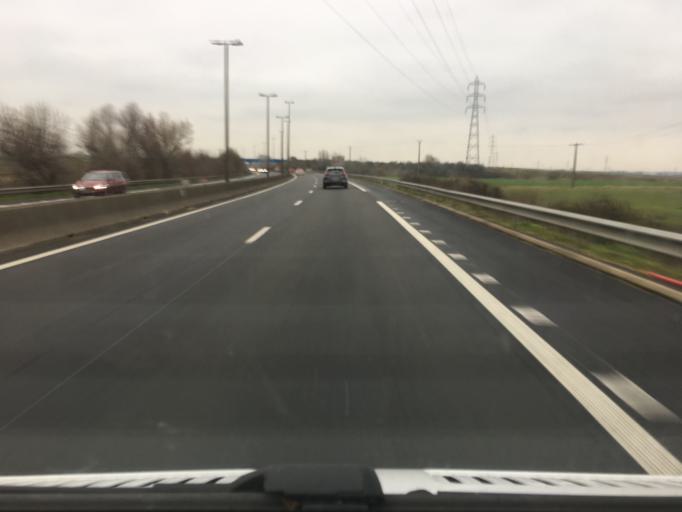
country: FR
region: Nord-Pas-de-Calais
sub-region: Departement du Nord
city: Bourbourg
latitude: 50.9598
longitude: 2.2045
